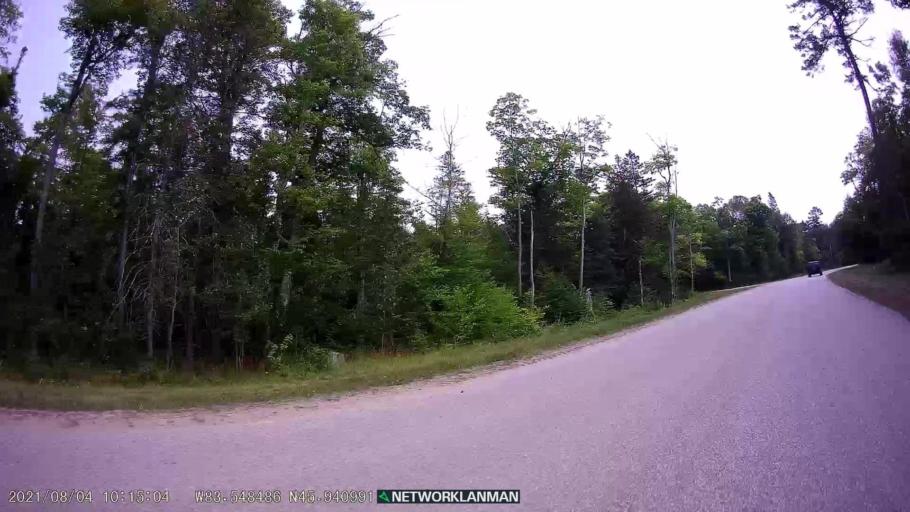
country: CA
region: Ontario
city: Thessalon
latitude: 45.9410
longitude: -83.5479
